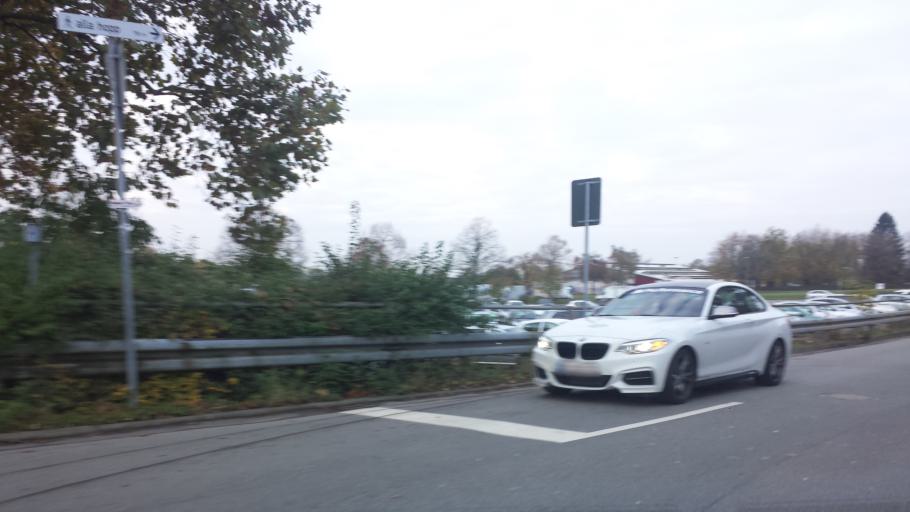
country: DE
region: Baden-Wuerttemberg
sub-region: Karlsruhe Region
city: Heidelberg
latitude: 49.3913
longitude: 8.6752
